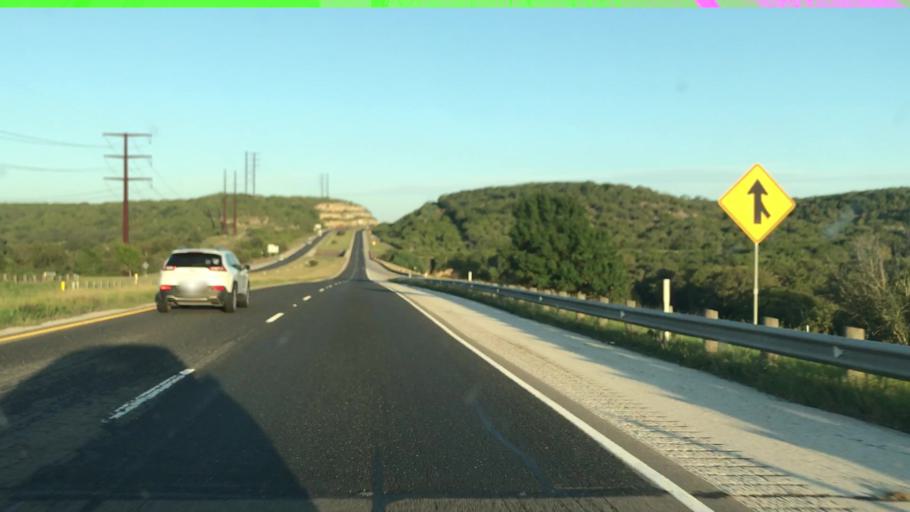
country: US
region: Texas
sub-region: Kerr County
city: Kerrville
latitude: 30.0704
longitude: -99.1108
